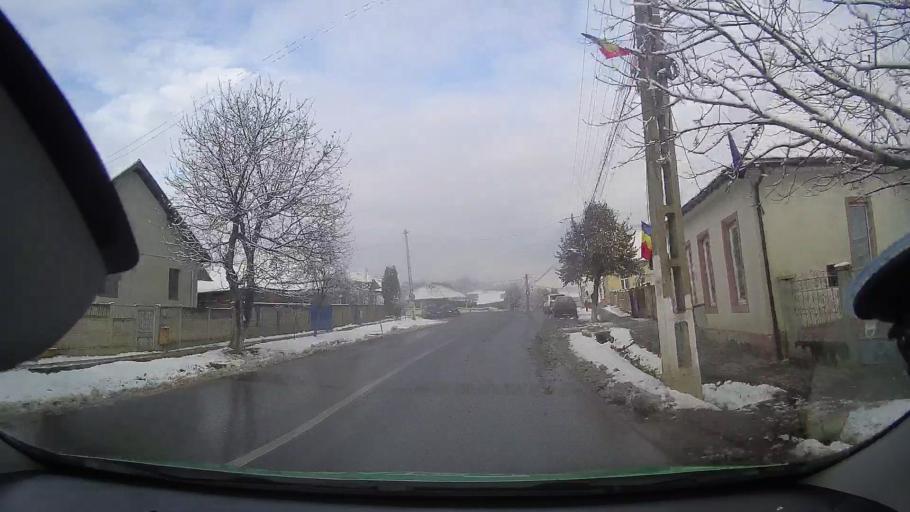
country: RO
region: Mures
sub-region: Comuna Atintis
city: Atintis
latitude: 46.4301
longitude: 24.1049
